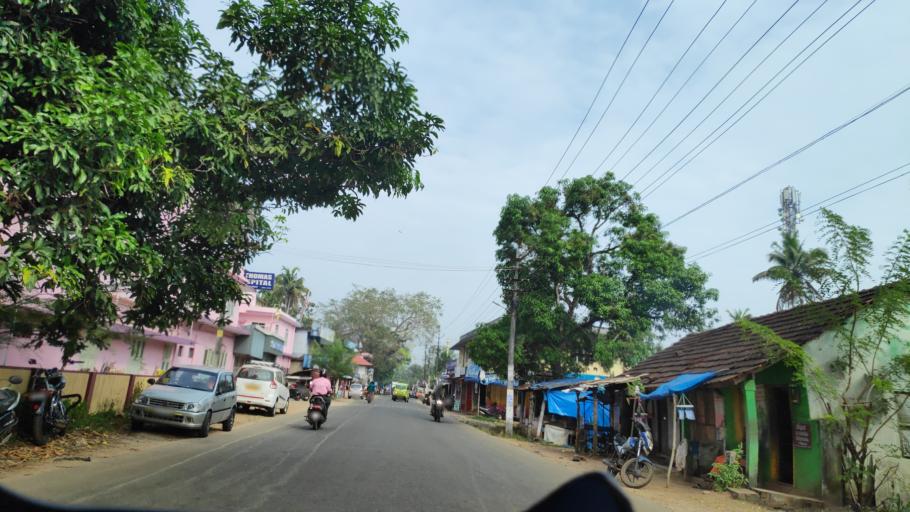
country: IN
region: Kerala
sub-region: Kottayam
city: Vaikam
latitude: 9.7628
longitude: 76.3629
